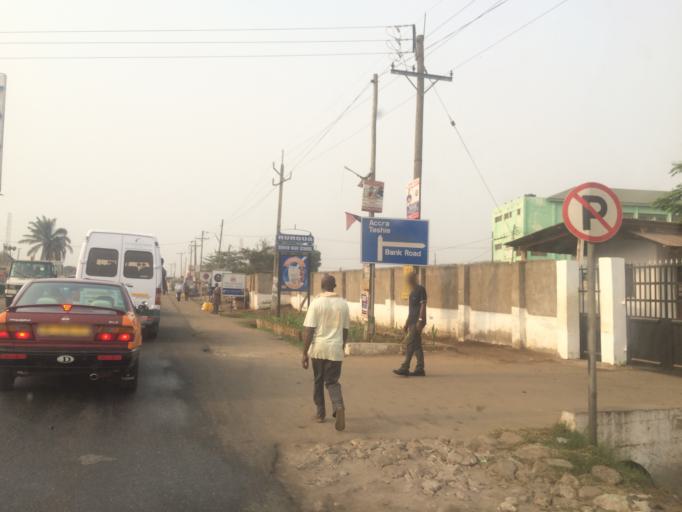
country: GH
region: Greater Accra
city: Nungua
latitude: 5.6027
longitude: -0.0791
